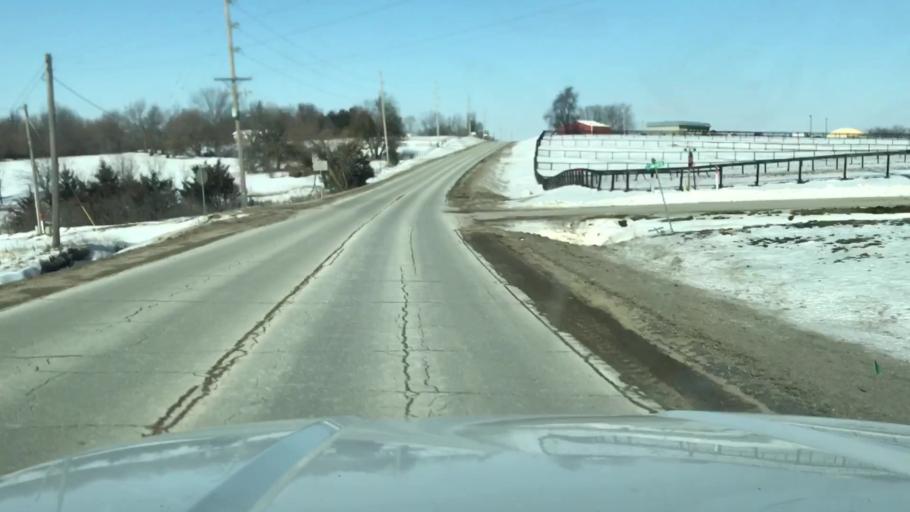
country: US
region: Missouri
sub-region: Andrew County
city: Savannah
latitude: 39.9517
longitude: -94.8466
